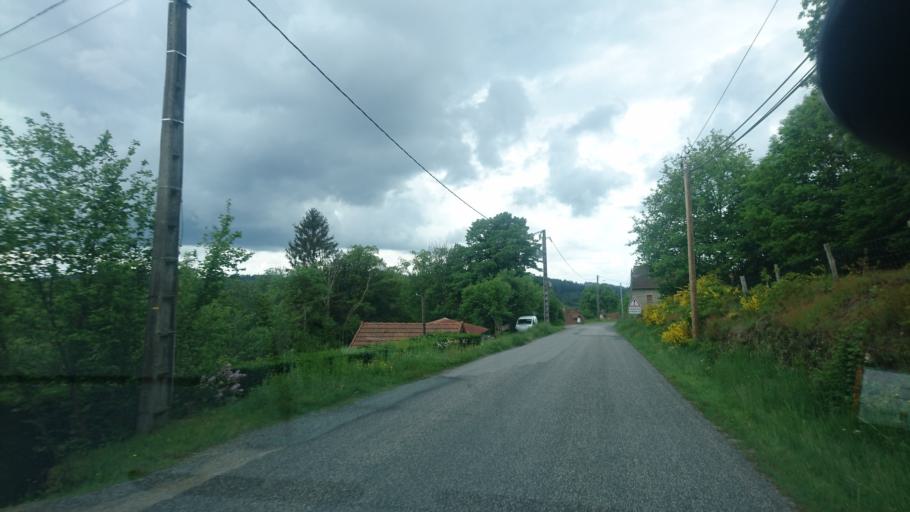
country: FR
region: Limousin
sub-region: Departement de la Haute-Vienne
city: Peyrat-le-Chateau
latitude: 45.8311
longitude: 1.8829
